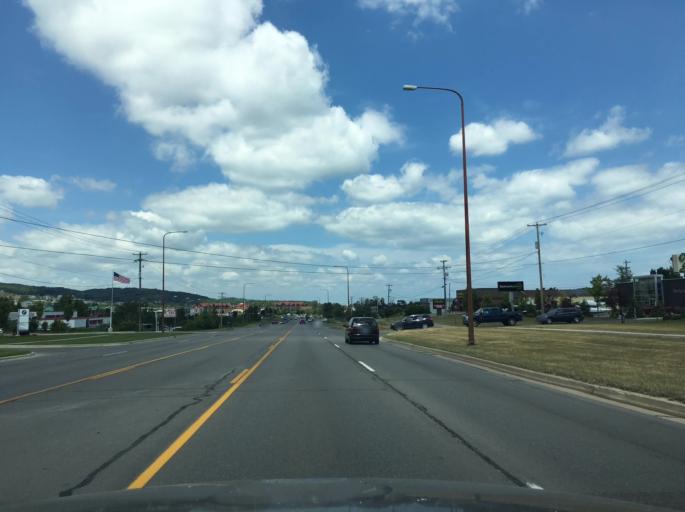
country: US
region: Michigan
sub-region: Grand Traverse County
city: Traverse City
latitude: 44.7283
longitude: -85.6461
